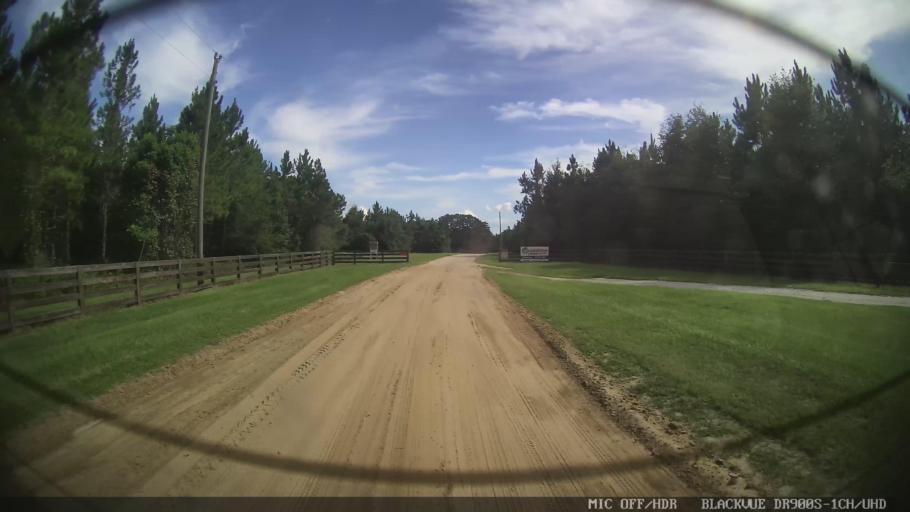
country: US
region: Georgia
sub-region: Echols County
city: Statenville
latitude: 30.6136
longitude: -83.2017
